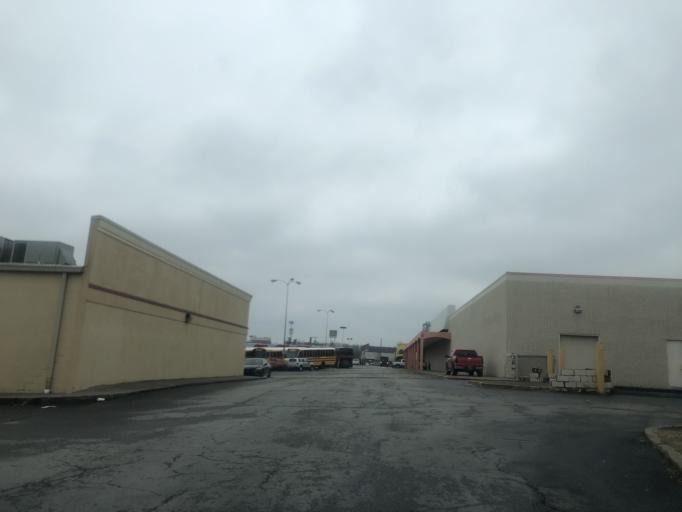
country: US
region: Tennessee
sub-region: Davidson County
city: Lakewood
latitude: 36.1484
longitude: -86.6678
